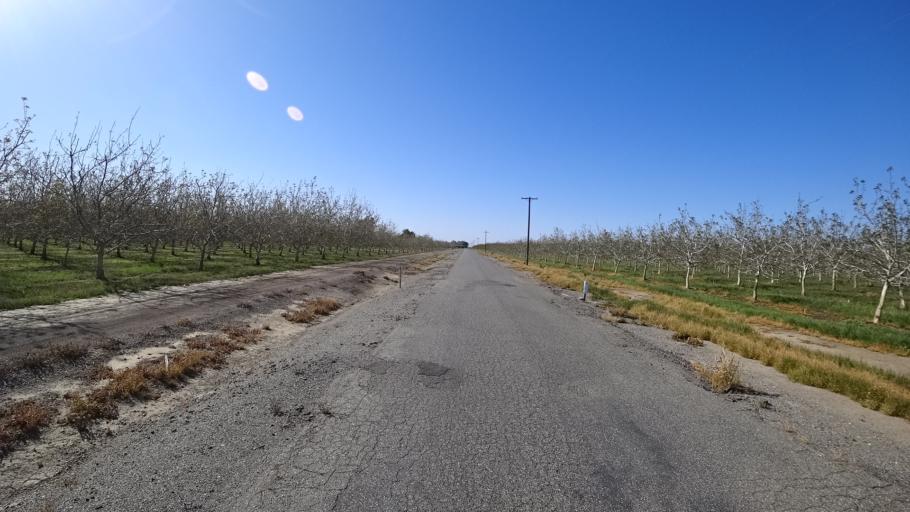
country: US
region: California
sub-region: Glenn County
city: Hamilton City
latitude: 39.6890
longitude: -122.0743
